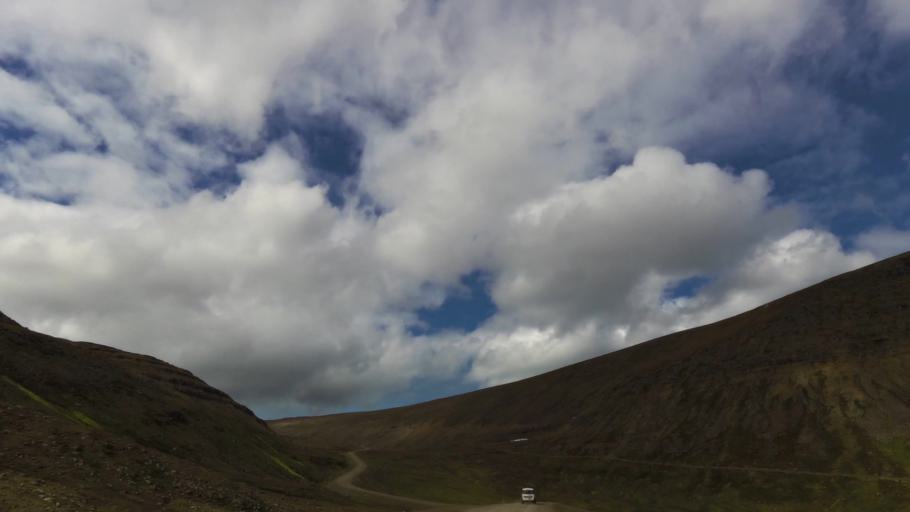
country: IS
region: Westfjords
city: Isafjoerdur
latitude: 66.1665
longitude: -23.3413
